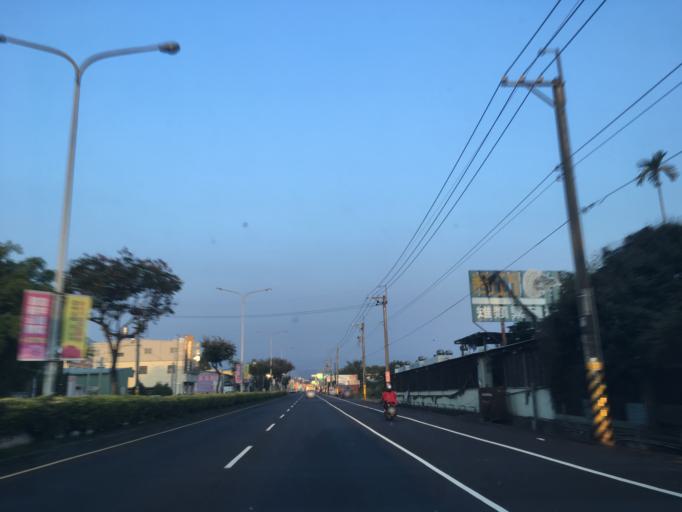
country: TW
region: Taiwan
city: Zhongxing New Village
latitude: 23.9878
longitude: 120.6739
